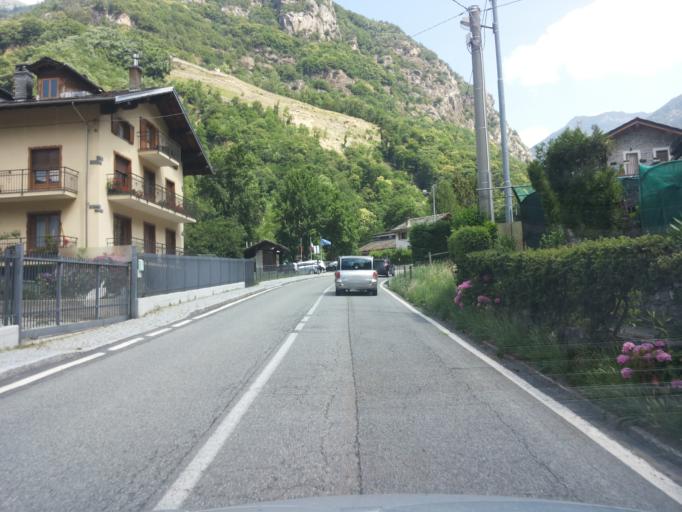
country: IT
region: Aosta Valley
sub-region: Valle d'Aosta
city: Lillianes
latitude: 45.6347
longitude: 7.8472
